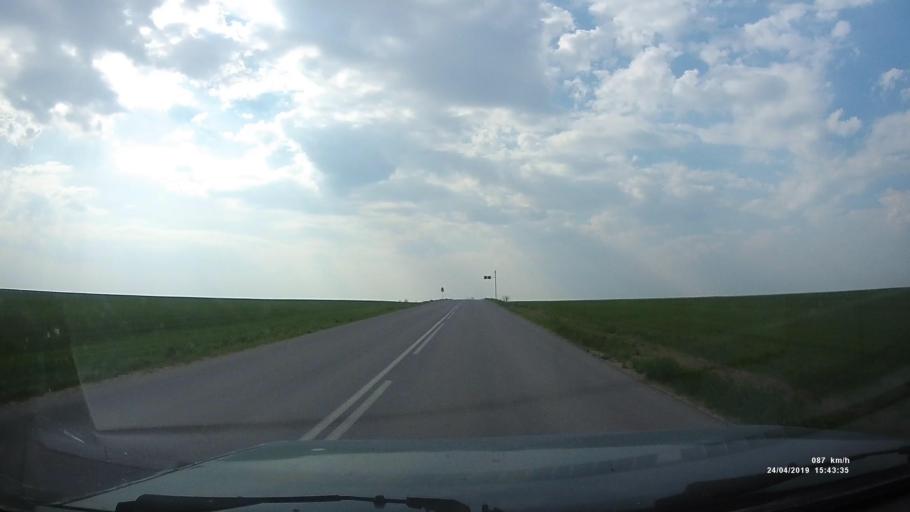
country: RU
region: Kalmykiya
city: Yashalta
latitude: 46.5836
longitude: 42.7699
